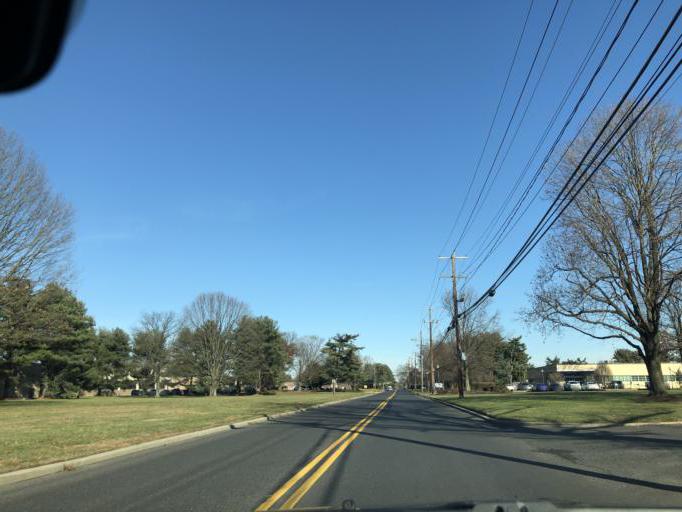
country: US
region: New Jersey
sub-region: Burlington County
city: Moorestown-Lenola
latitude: 39.9673
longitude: -74.9714
